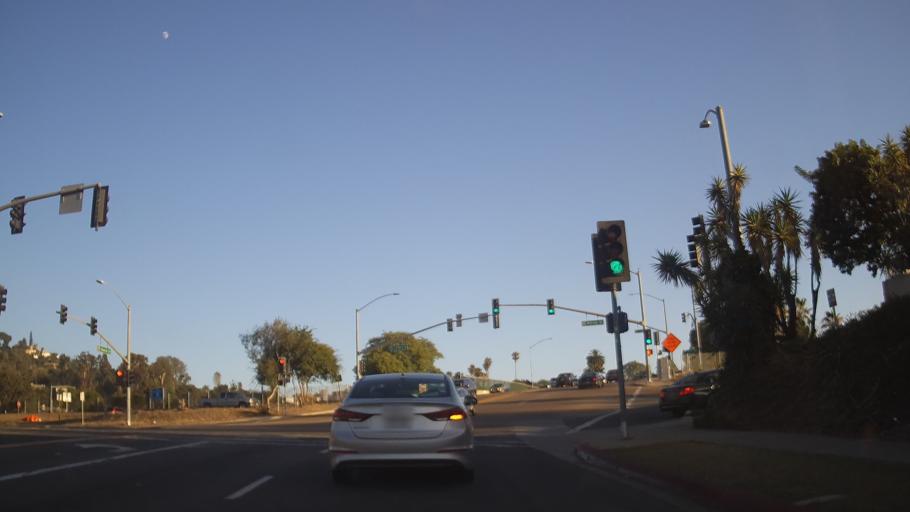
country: US
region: California
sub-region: San Diego County
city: La Mesa
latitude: 32.7807
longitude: -116.9972
